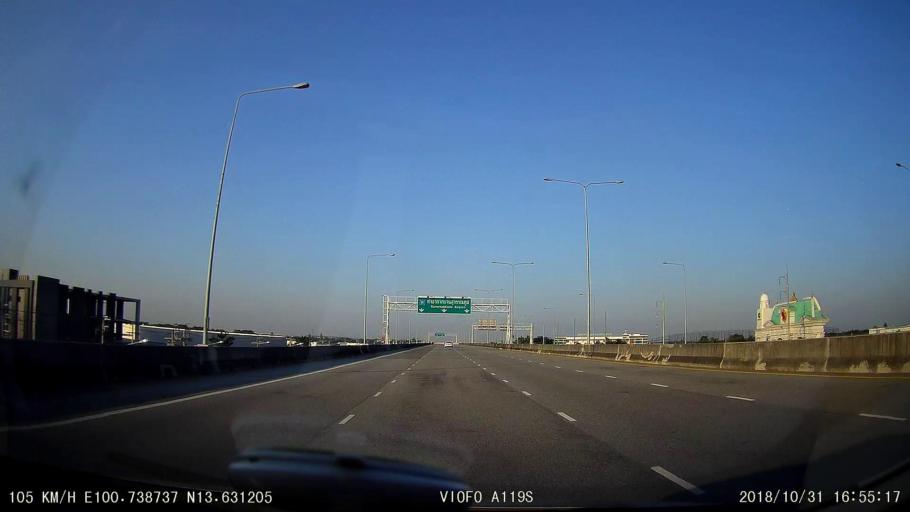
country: TH
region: Samut Prakan
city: Bang Bo District
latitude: 13.6313
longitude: 100.7388
